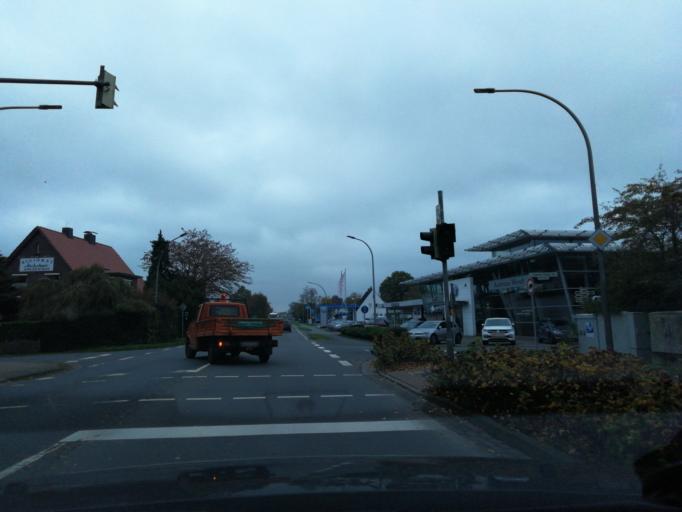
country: DE
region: Lower Saxony
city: Schortens
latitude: 53.5433
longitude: 7.9514
